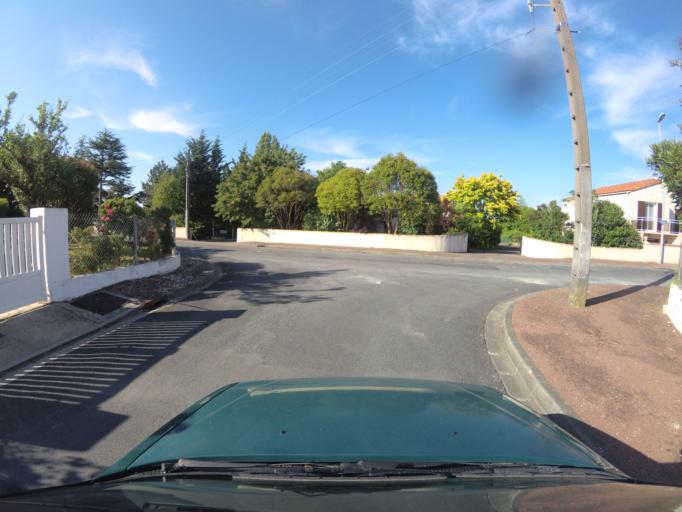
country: FR
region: Poitou-Charentes
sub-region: Departement de la Charente-Maritime
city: Royan
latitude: 45.6354
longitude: -1.0243
